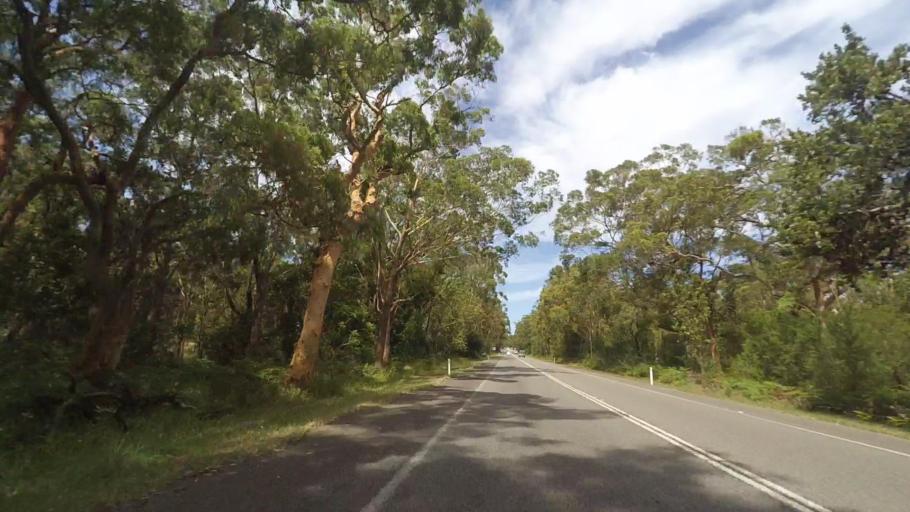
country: AU
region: New South Wales
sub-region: Port Stephens Shire
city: Medowie
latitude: -32.7933
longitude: 151.9460
